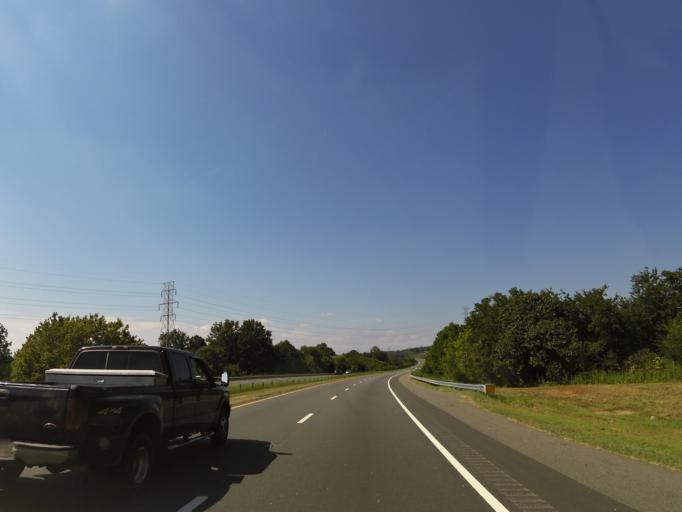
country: US
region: North Carolina
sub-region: Catawba County
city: Maiden
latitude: 35.5984
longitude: -81.2682
